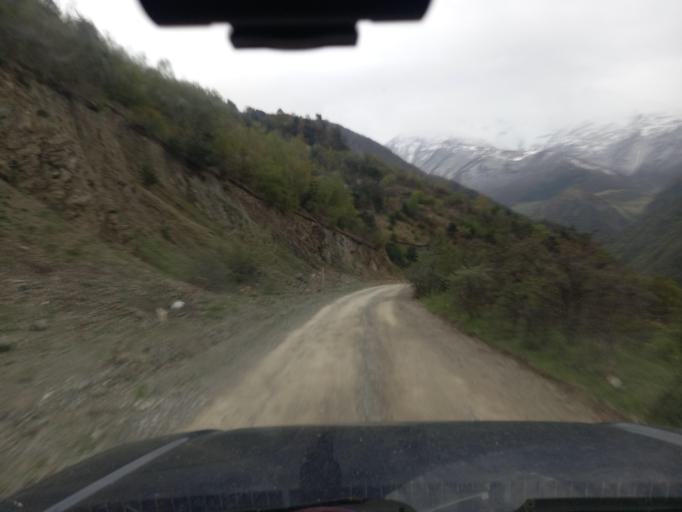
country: RU
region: North Ossetia
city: Mizur
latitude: 42.8546
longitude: 44.1647
